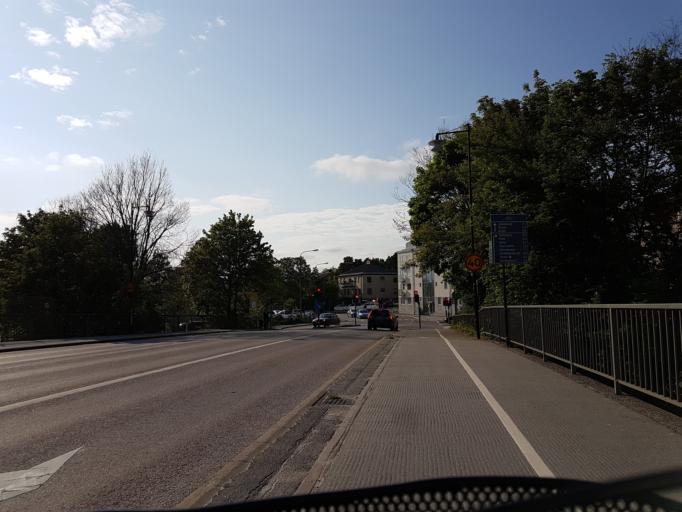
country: SE
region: Stockholm
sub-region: Sundbybergs Kommun
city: Sundbyberg
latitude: 59.3650
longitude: 17.9571
